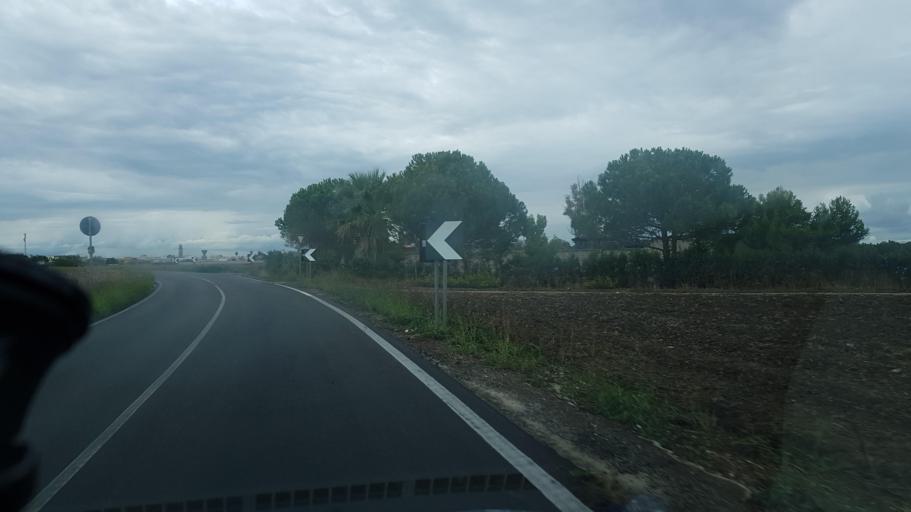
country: IT
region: Apulia
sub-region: Provincia di Lecce
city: Salice Salentino
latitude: 40.3782
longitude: 17.9758
